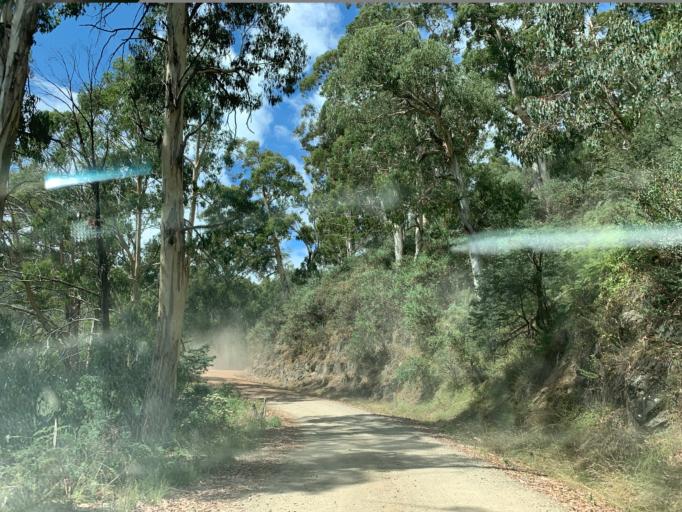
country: AU
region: Victoria
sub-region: Mansfield
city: Mansfield
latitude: -37.0927
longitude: 146.5367
